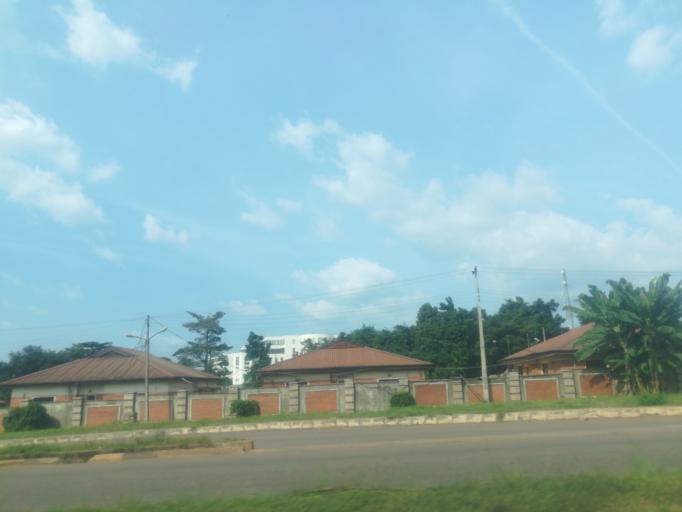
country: NG
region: Ogun
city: Abeokuta
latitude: 7.1235
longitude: 3.3635
